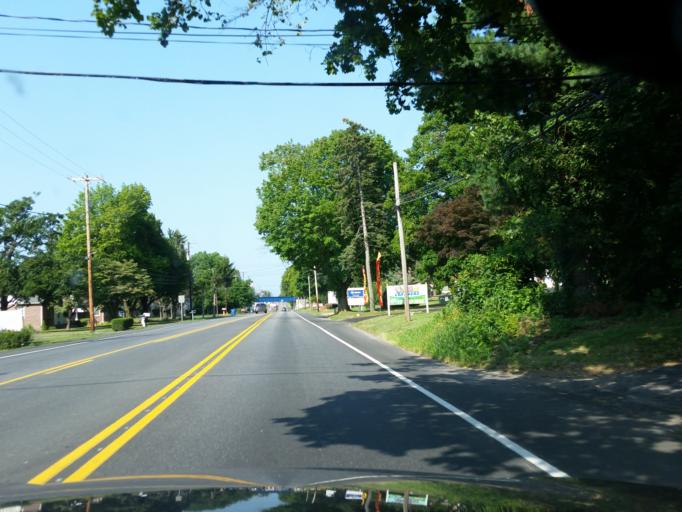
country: US
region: Pennsylvania
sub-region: Cumberland County
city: Shiremanstown
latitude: 40.2256
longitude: -76.9709
